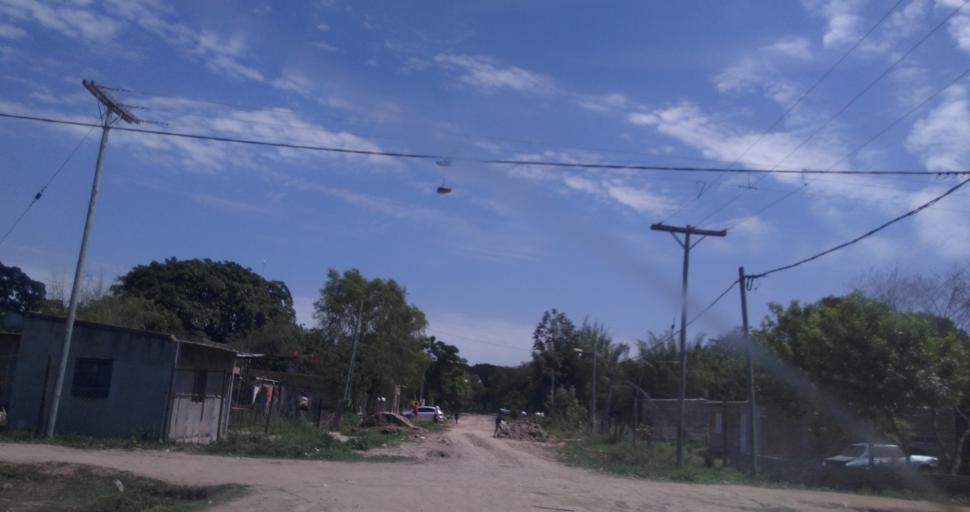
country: AR
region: Chaco
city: Resistencia
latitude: -27.4189
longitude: -58.9817
